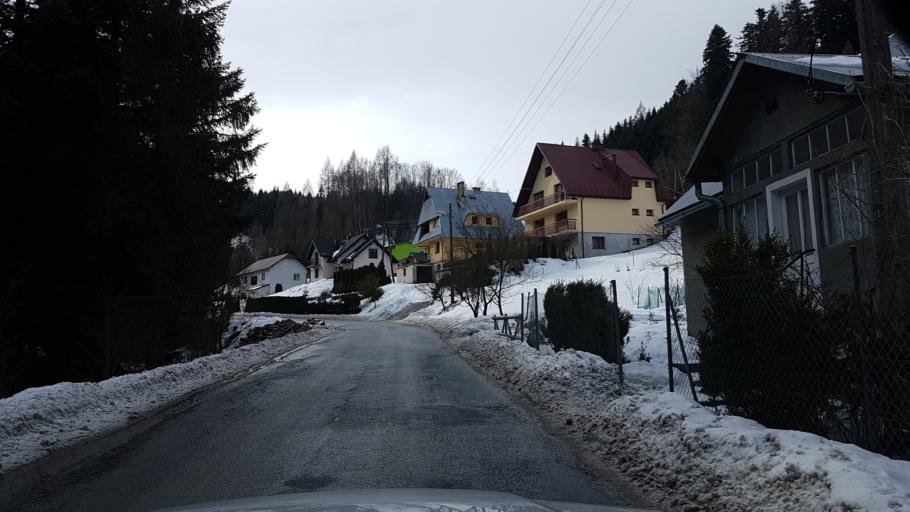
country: PL
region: Lesser Poland Voivodeship
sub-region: Powiat nowosadecki
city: Piwniczna-Zdroj
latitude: 49.4242
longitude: 20.6522
